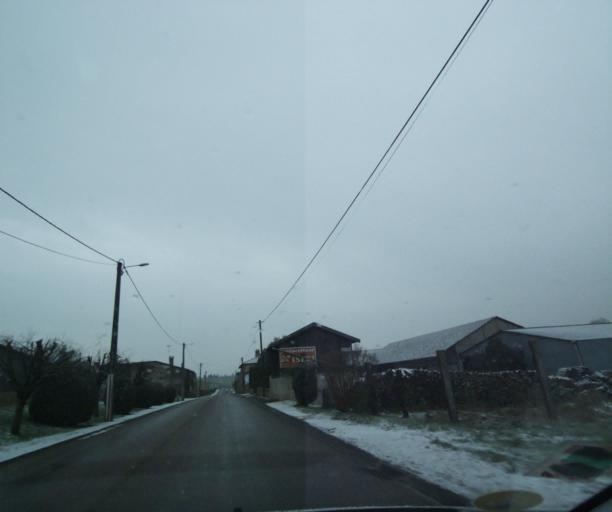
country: FR
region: Champagne-Ardenne
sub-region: Departement de la Haute-Marne
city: Wassy
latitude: 48.4552
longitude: 4.9628
